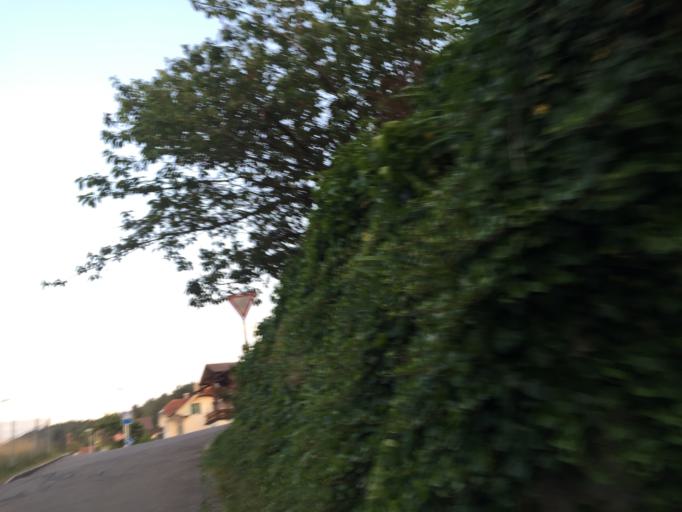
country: CH
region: Bern
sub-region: Bern-Mittelland District
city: Bern
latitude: 46.9308
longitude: 7.4379
